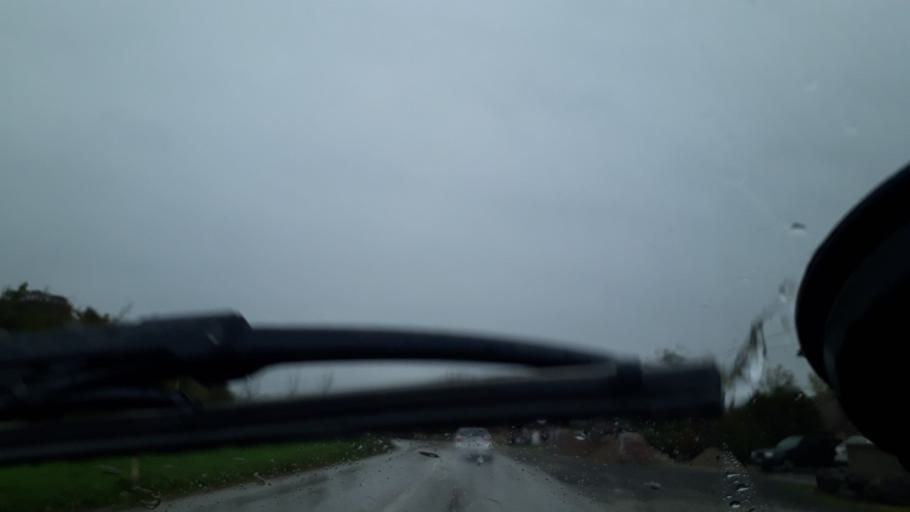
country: BA
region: Republika Srpska
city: Maglajani
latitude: 44.8670
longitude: 17.4110
